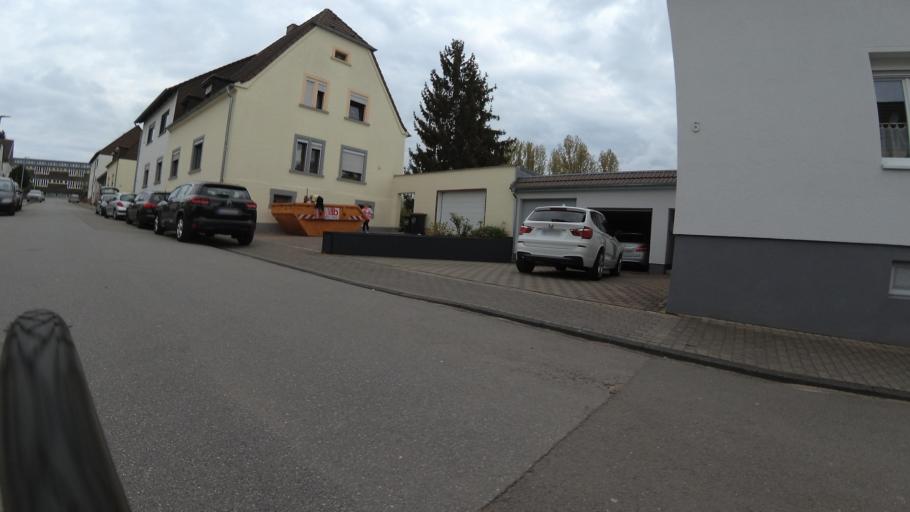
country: DE
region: Rheinland-Pfalz
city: Zweibrucken
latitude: 49.2429
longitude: 7.3506
